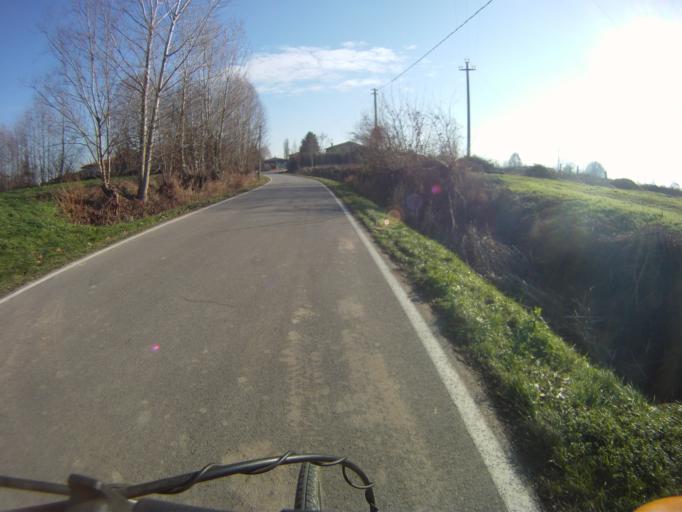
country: IT
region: Veneto
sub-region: Provincia di Padova
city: Polverara
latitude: 45.3216
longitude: 11.9711
